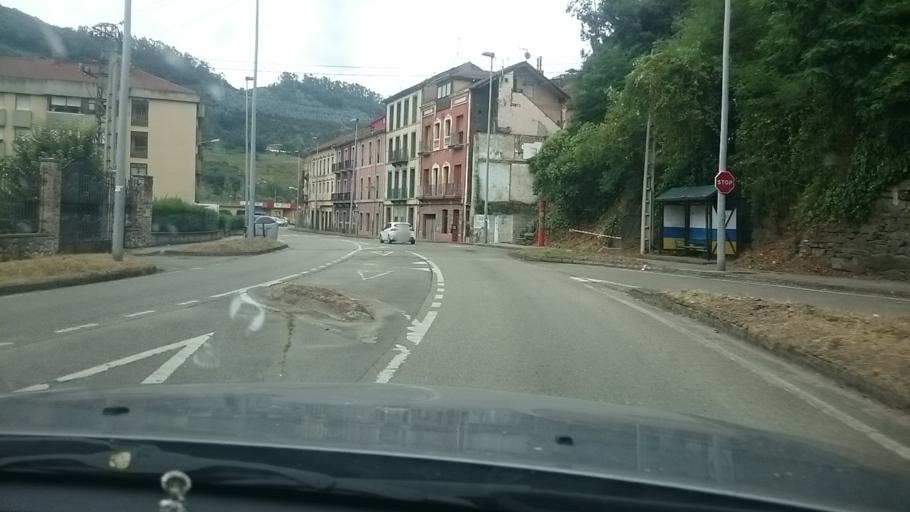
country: ES
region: Asturias
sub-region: Province of Asturias
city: Mieres
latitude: 43.2121
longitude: -5.7825
